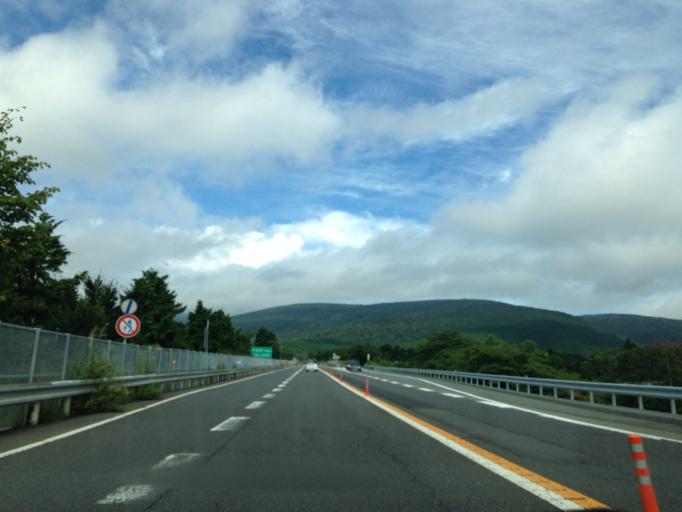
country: JP
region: Shizuoka
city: Gotemba
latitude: 35.3610
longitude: 138.8634
